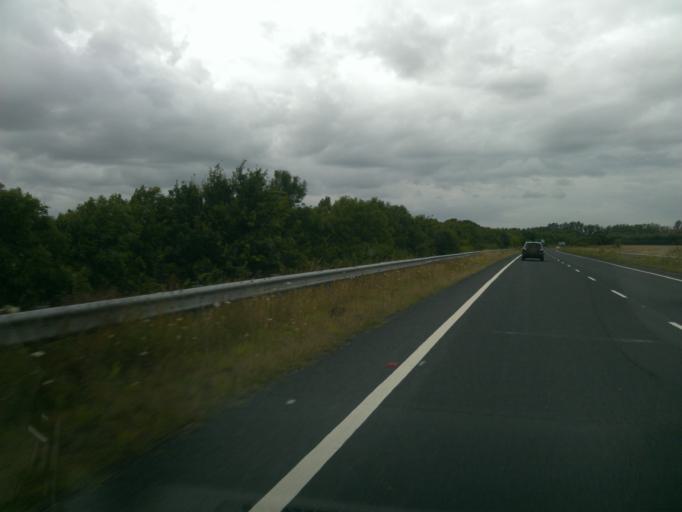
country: GB
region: England
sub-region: Essex
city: Great Bentley
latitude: 51.8535
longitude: 1.1012
